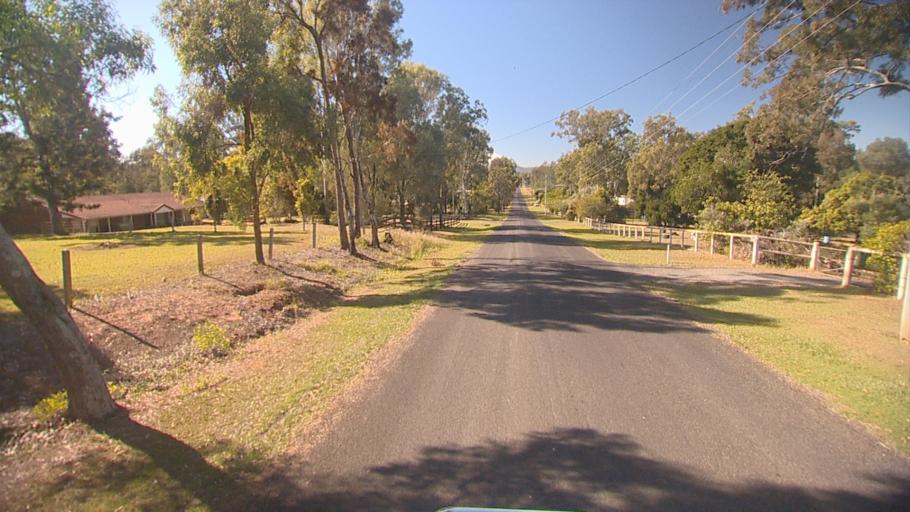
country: AU
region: Queensland
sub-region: Logan
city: Chambers Flat
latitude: -27.7565
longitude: 153.0703
